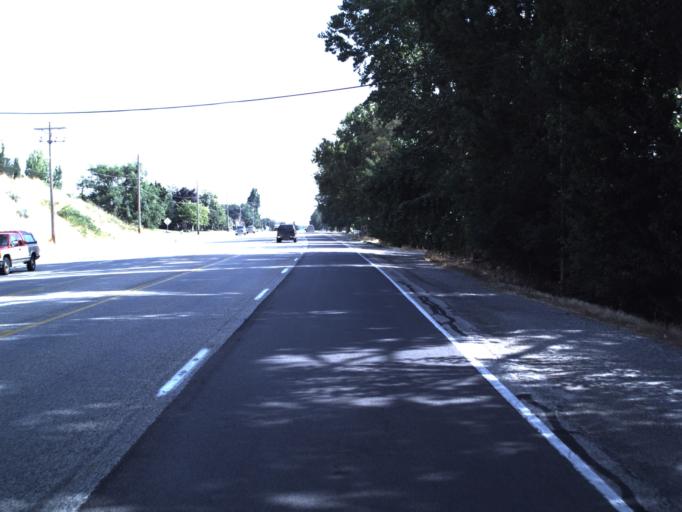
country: US
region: Utah
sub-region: Box Elder County
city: Willard
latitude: 41.4137
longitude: -112.0363
